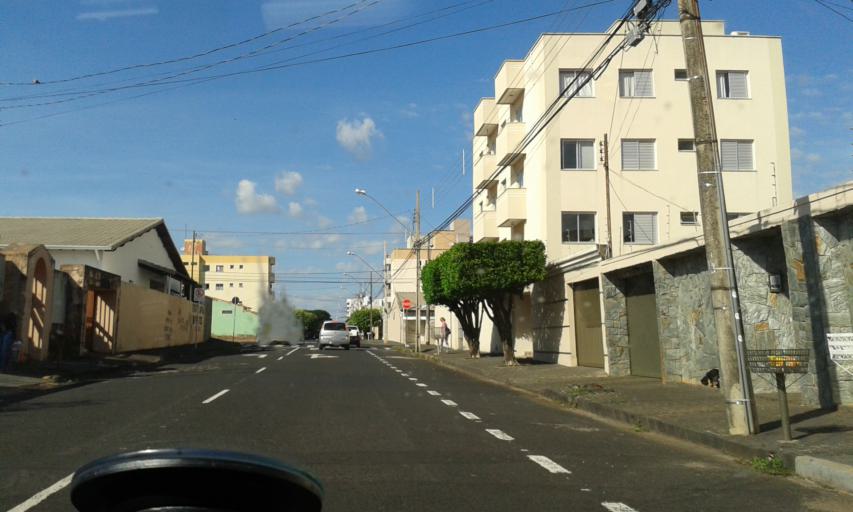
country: BR
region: Minas Gerais
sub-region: Uberlandia
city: Uberlandia
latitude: -18.9204
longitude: -48.2461
